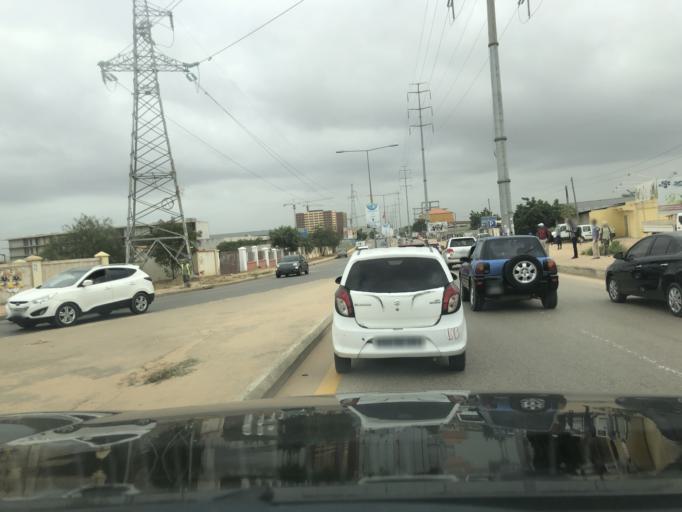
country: AO
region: Luanda
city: Luanda
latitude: -8.9746
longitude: 13.2103
